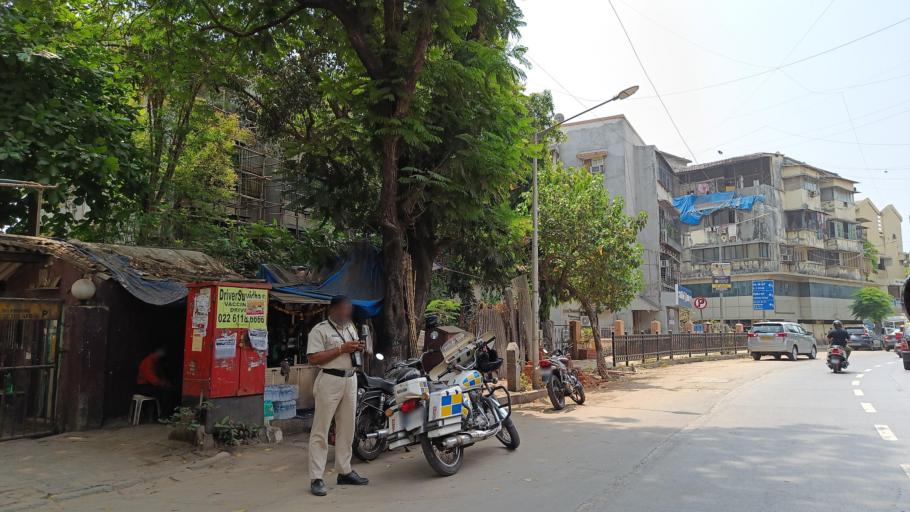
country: IN
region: Maharashtra
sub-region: Mumbai Suburban
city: Mumbai
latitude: 19.0876
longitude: 72.8273
